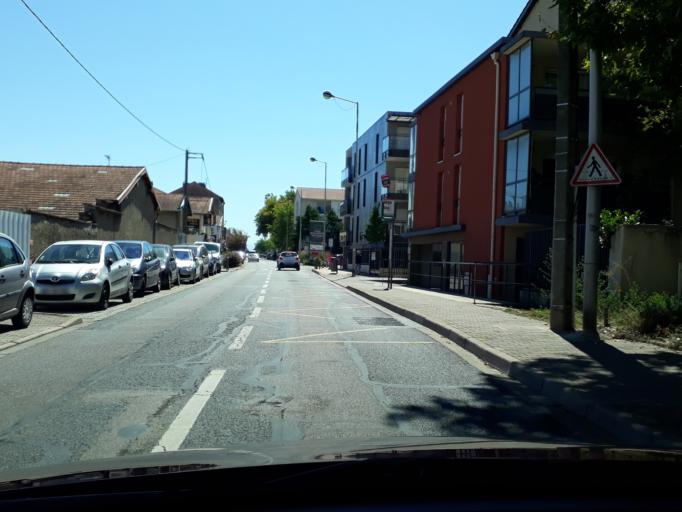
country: FR
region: Rhone-Alpes
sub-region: Departement du Rhone
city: Saint-Priest
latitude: 45.6917
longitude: 4.9341
